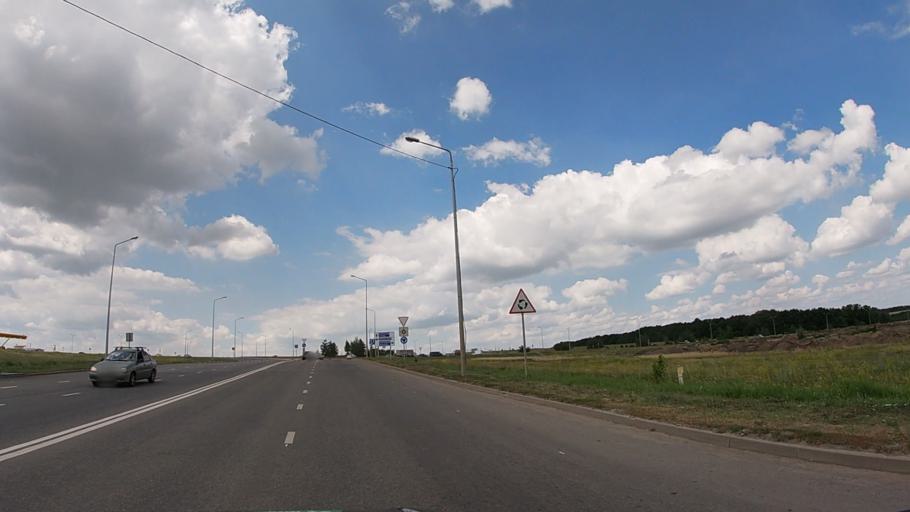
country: RU
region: Belgorod
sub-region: Belgorodskiy Rayon
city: Belgorod
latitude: 50.5940
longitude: 36.5337
